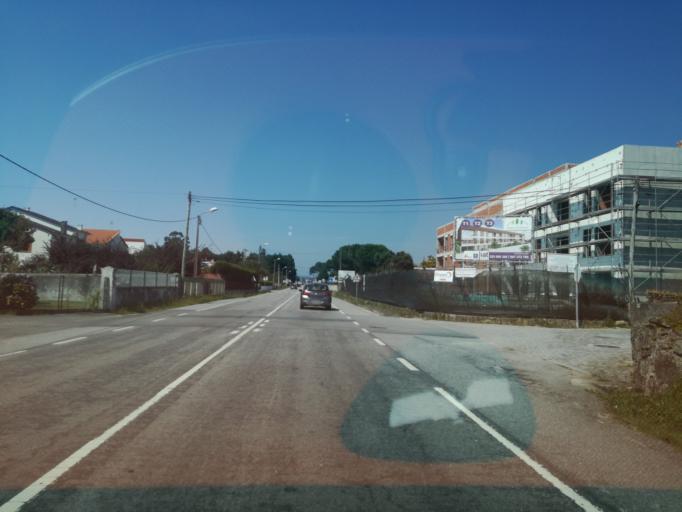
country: PT
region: Braga
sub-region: Esposende
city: Esposende
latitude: 41.5424
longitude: -8.7821
